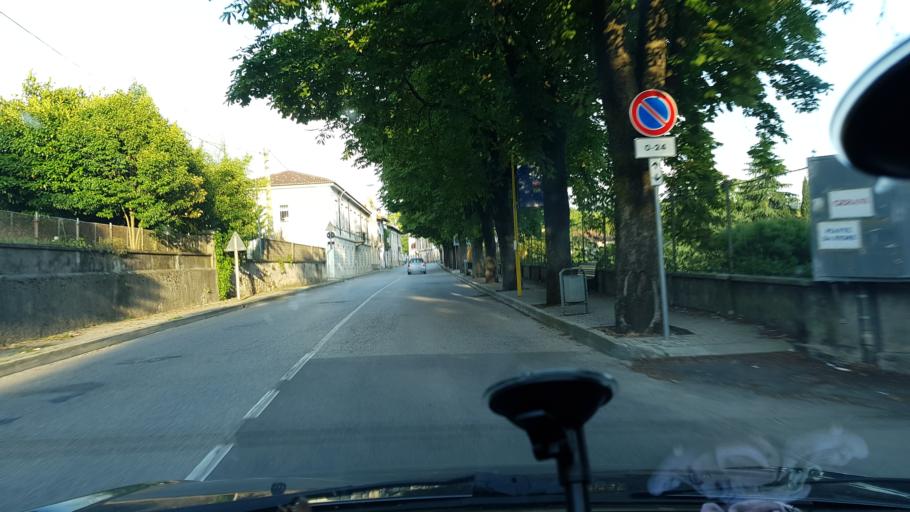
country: IT
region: Friuli Venezia Giulia
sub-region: Provincia di Gorizia
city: Gradisca d'Isonzo
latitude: 45.8935
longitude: 13.4968
